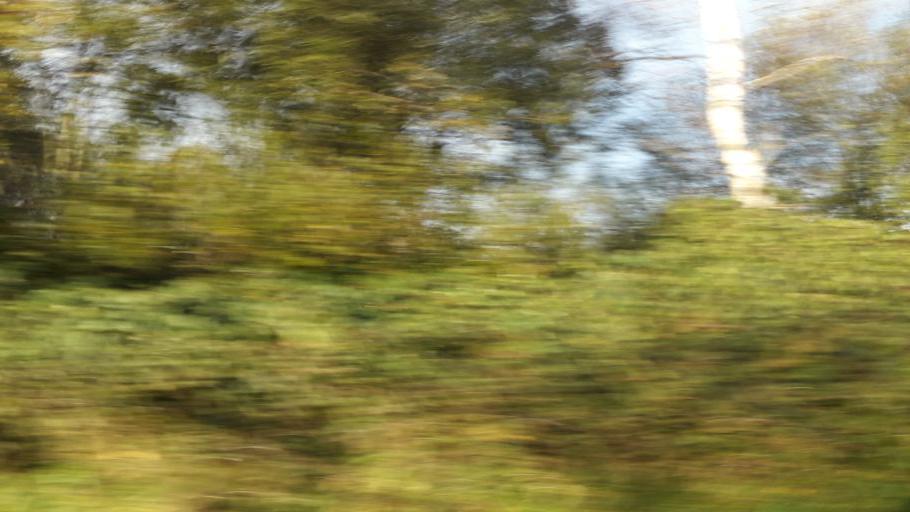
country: IE
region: Leinster
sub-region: An Longfort
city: Lanesborough
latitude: 53.7516
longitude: -7.9582
